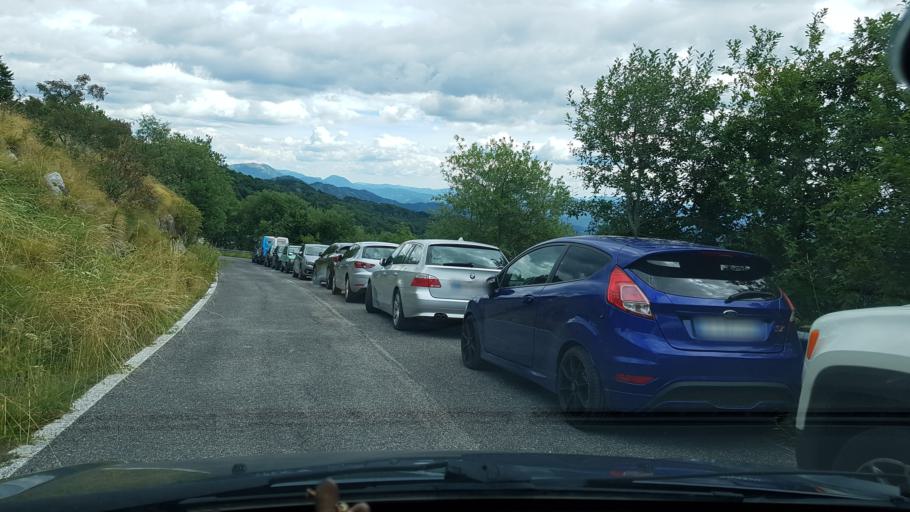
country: IT
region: Friuli Venezia Giulia
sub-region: Provincia di Udine
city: Savogna
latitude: 46.2021
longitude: 13.5392
